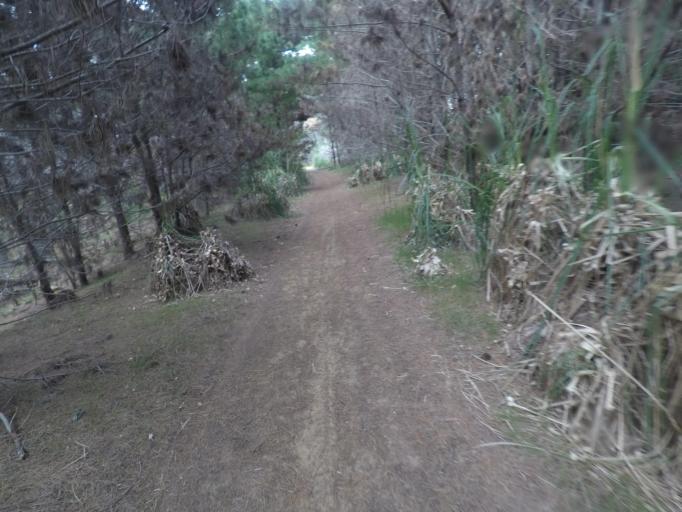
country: NZ
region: Auckland
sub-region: Auckland
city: Parakai
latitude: -36.6040
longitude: 174.2721
